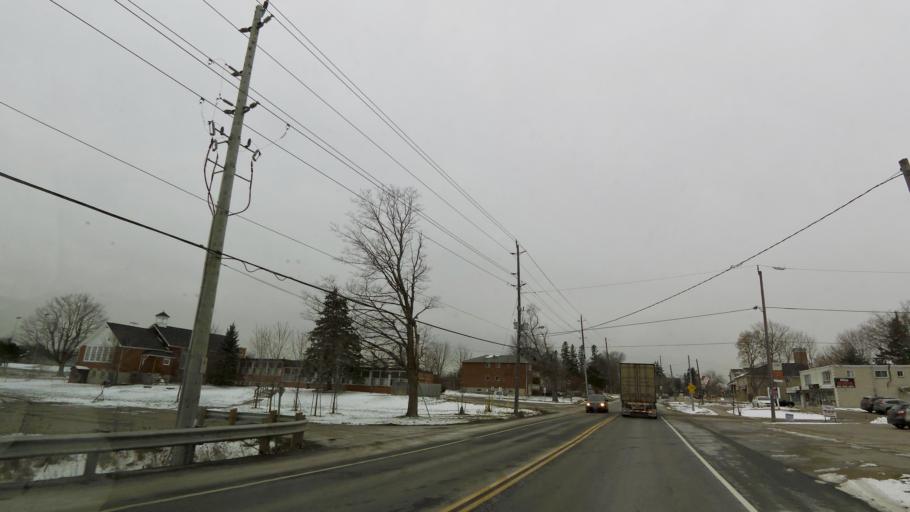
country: CA
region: Ontario
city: Vaughan
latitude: 43.9027
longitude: -79.6479
